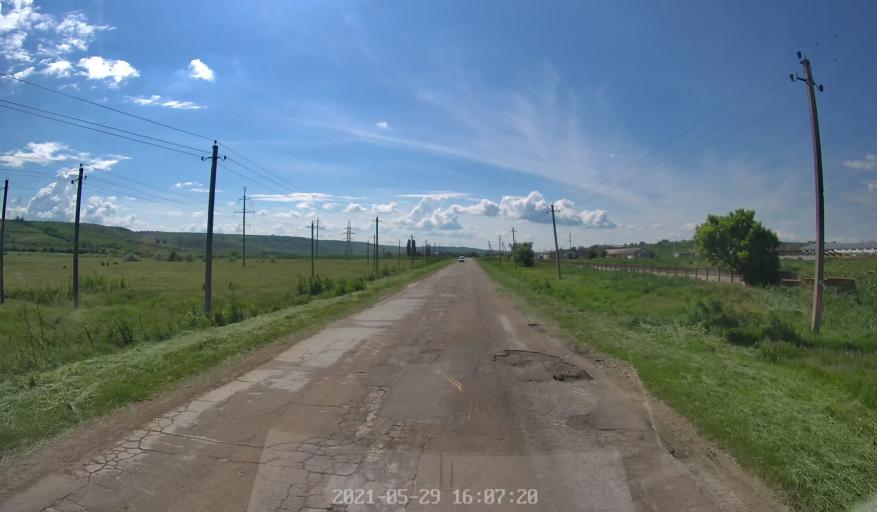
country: MD
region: Chisinau
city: Singera
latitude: 46.8162
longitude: 28.9021
